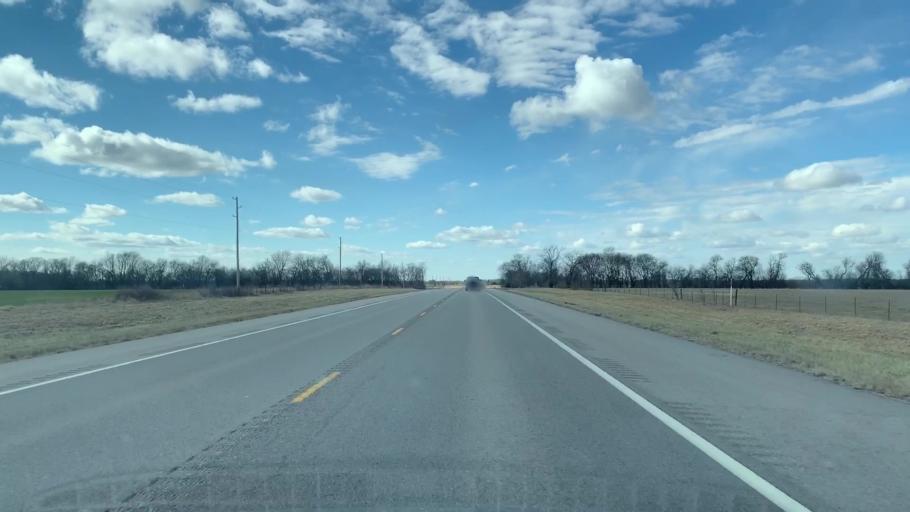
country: US
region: Kansas
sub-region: Labette County
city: Oswego
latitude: 37.3402
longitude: -95.0370
